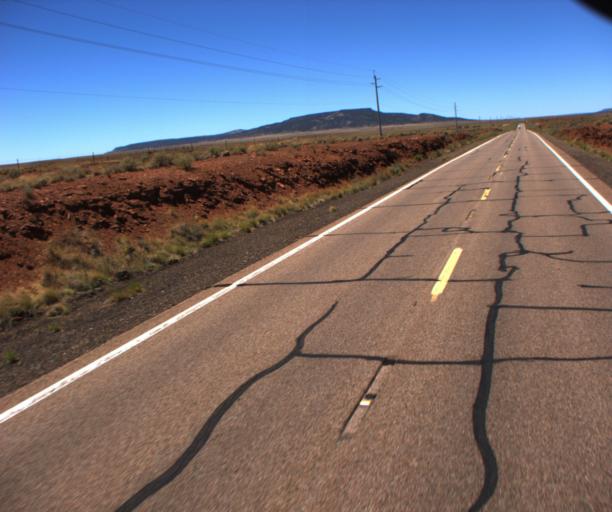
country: US
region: Arizona
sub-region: Coconino County
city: LeChee
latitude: 34.9136
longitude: -110.8319
